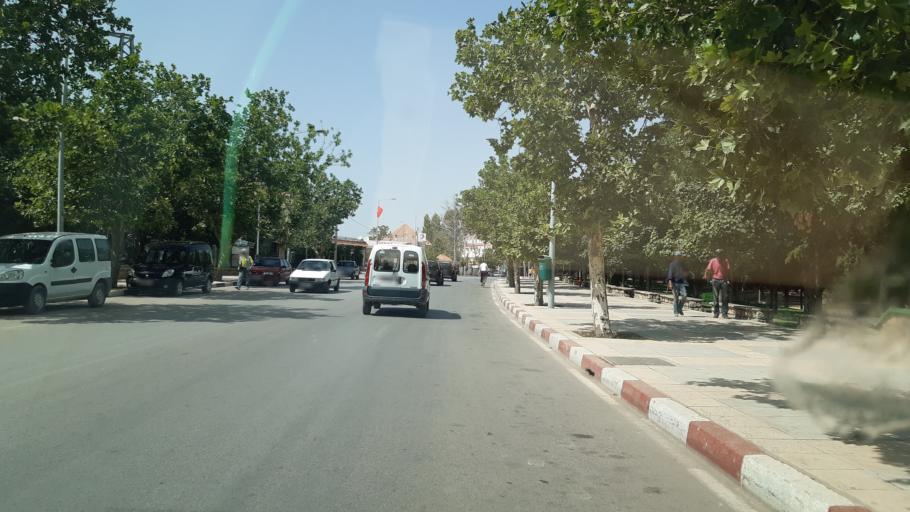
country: MA
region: Fes-Boulemane
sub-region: Sefrou
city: Bhalil
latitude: 33.7296
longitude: -5.0105
